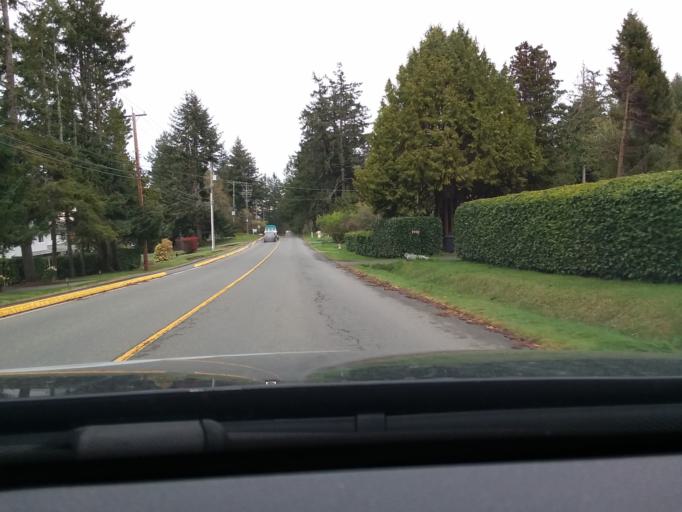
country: CA
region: British Columbia
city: North Saanich
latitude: 48.6175
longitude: -123.4199
